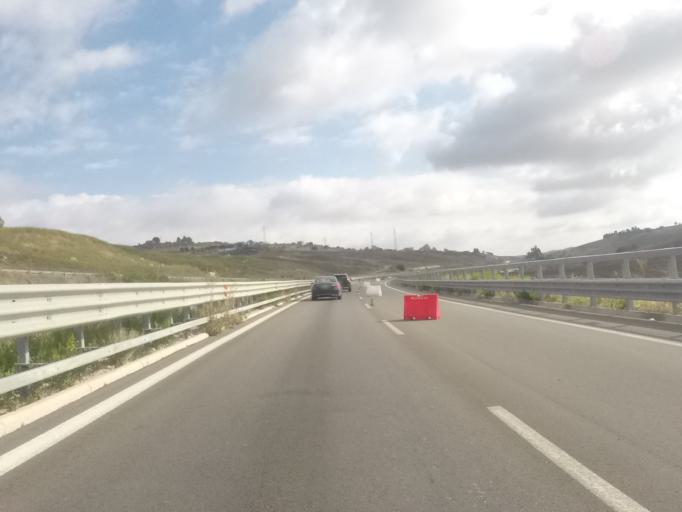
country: IT
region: Sicily
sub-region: Agrigento
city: Agrigento
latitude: 37.3374
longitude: 13.6229
